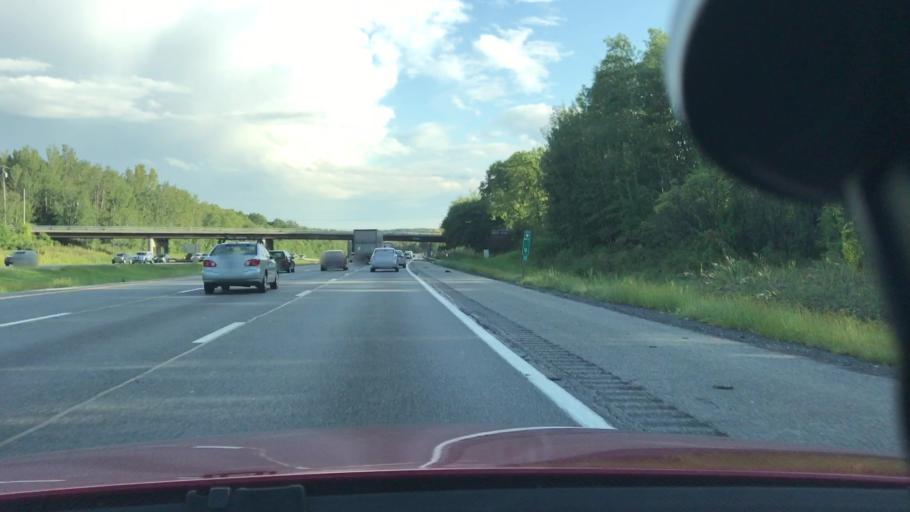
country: US
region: New York
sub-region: Albany County
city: Cohoes
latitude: 42.8020
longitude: -73.7653
